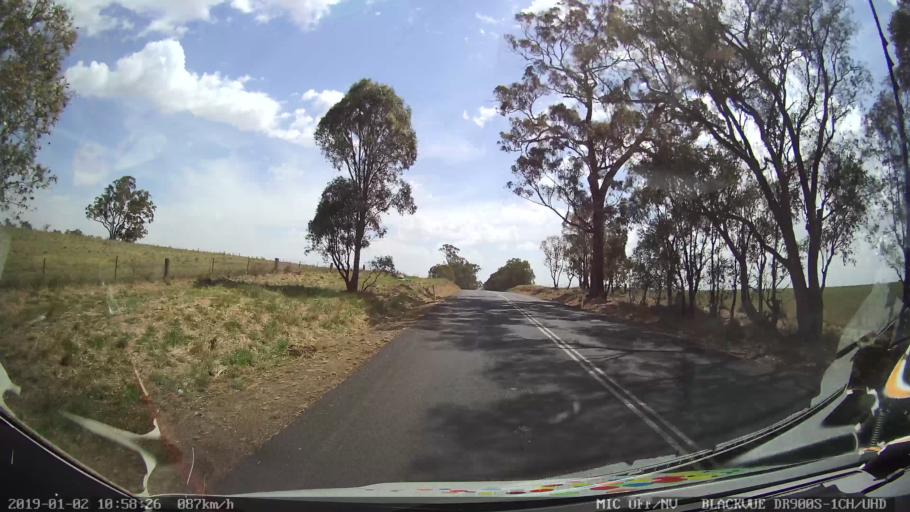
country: AU
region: New South Wales
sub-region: Cootamundra
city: Cootamundra
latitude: -34.6245
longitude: 148.2913
